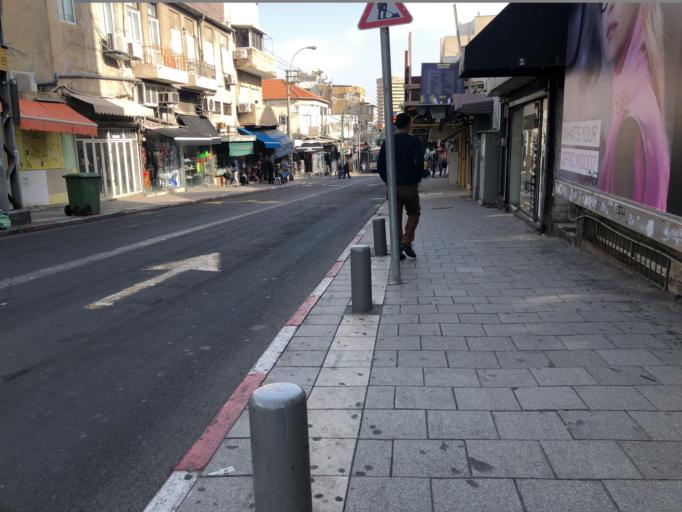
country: IL
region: Tel Aviv
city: Tel Aviv
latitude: 32.0698
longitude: 34.7707
